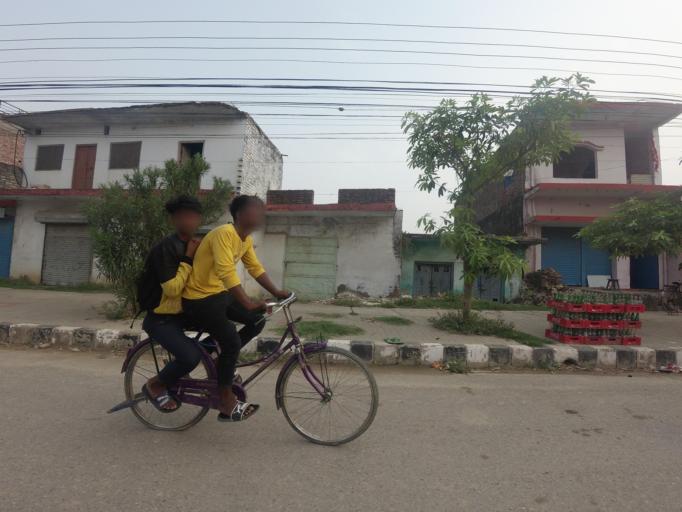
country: NP
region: Western Region
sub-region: Lumbini Zone
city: Bhairahawa
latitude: 27.5086
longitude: 83.4331
